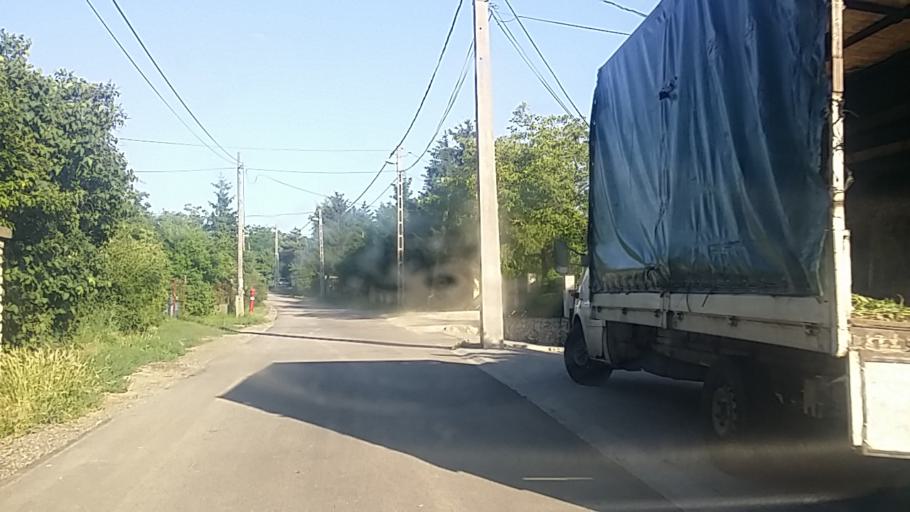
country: HU
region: Pest
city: Urom
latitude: 47.5834
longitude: 19.0072
